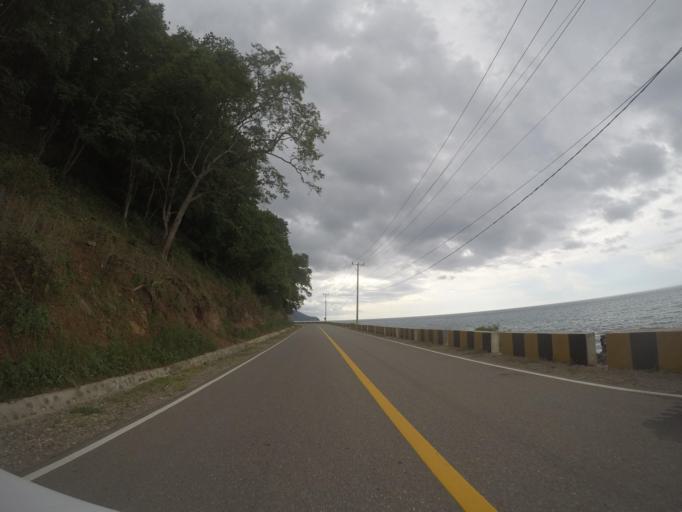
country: TL
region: Liquica
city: Maubara
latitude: -8.8044
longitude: 125.0909
